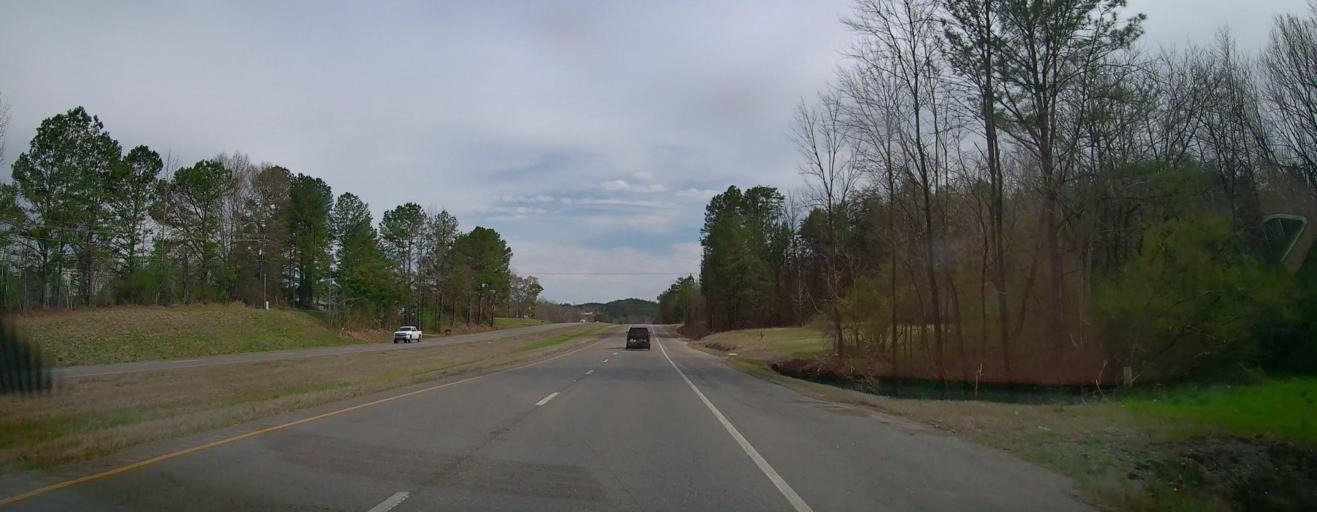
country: US
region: Alabama
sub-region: Walker County
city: Sumiton
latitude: 33.7901
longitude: -87.0916
